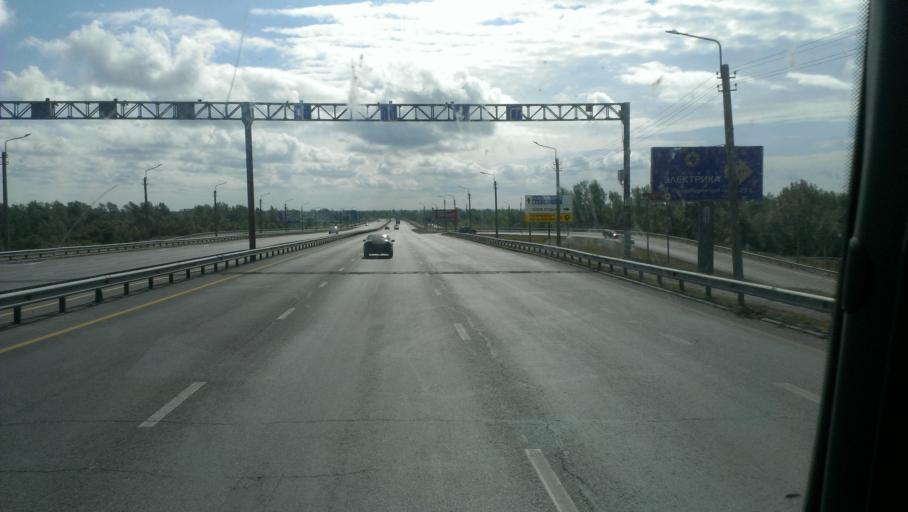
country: RU
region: Altai Krai
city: Zaton
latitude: 53.3205
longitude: 83.8120
